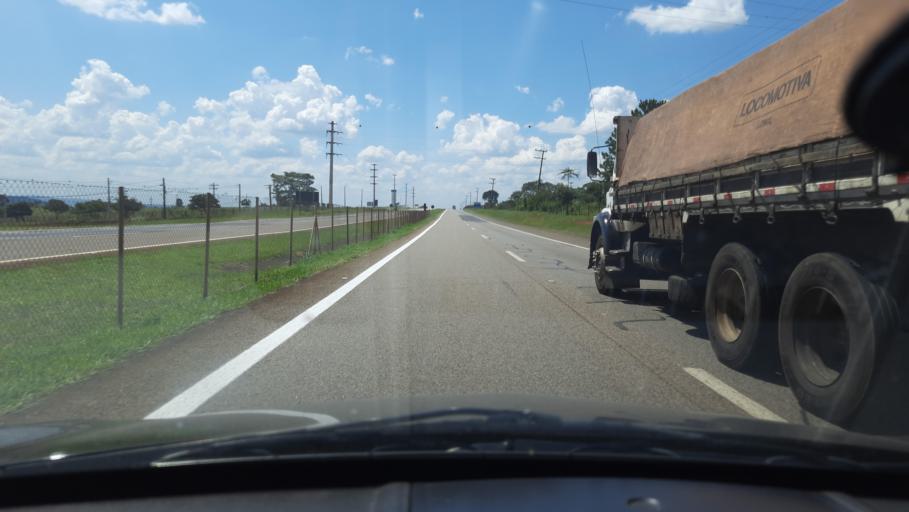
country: BR
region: Sao Paulo
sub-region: Casa Branca
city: Casa Branca
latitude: -21.7639
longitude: -47.0698
